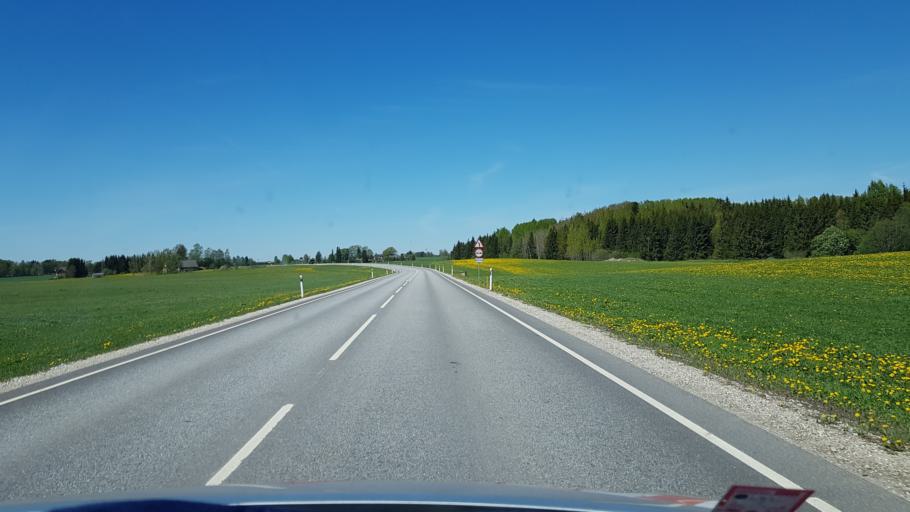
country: EE
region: Tartu
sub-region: Tartu linn
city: Tartu
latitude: 58.3882
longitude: 26.6011
